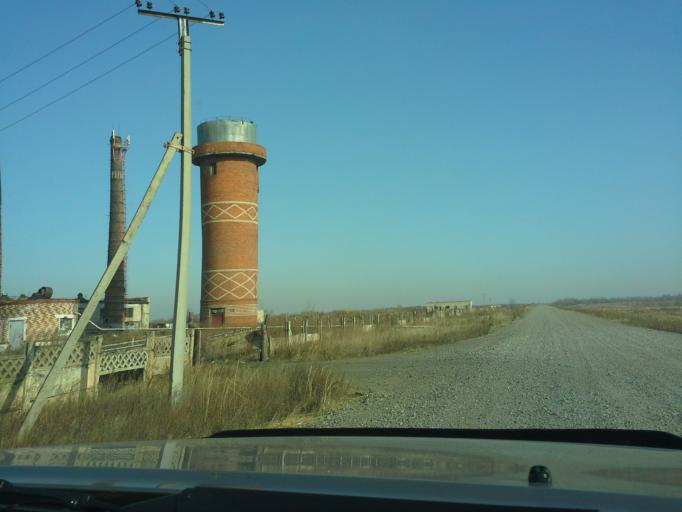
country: RU
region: Jewish Autonomous Oblast
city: Priamurskiy
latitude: 48.3584
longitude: 134.7968
